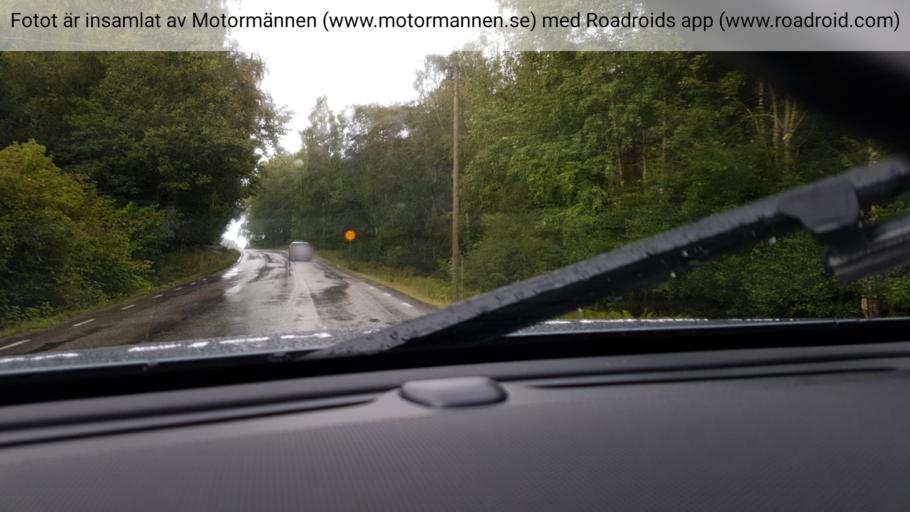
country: SE
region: Vaestra Goetaland
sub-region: Vanersborgs Kommun
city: Vanersborg
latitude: 58.3573
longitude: 12.2606
